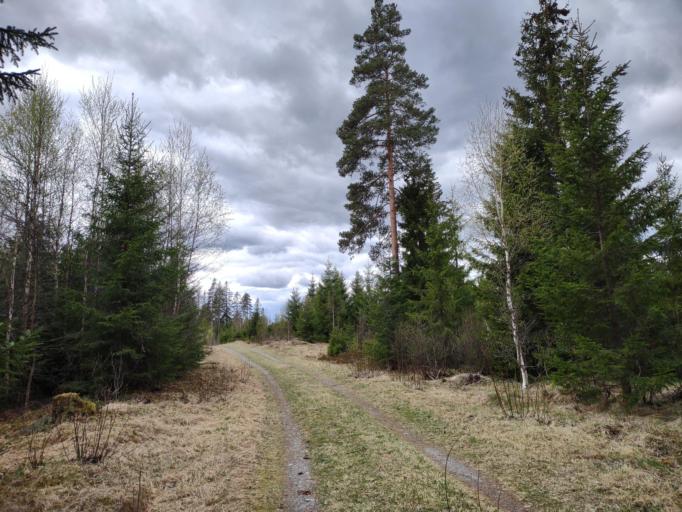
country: NO
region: Akershus
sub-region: Eidsvoll
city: Raholt
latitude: 60.2576
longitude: 11.1224
